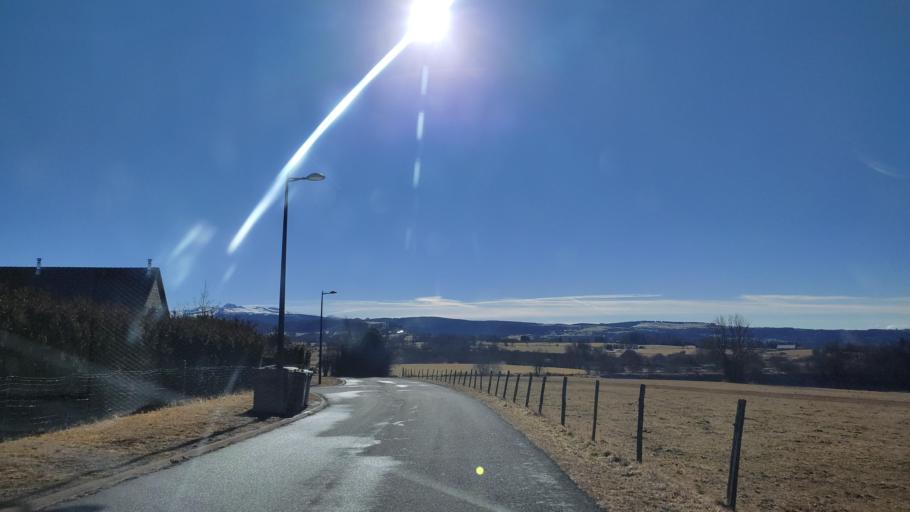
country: FR
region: Auvergne
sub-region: Departement du Puy-de-Dome
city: Saint-Sauves-d'Auvergne
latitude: 45.6451
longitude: 2.7014
